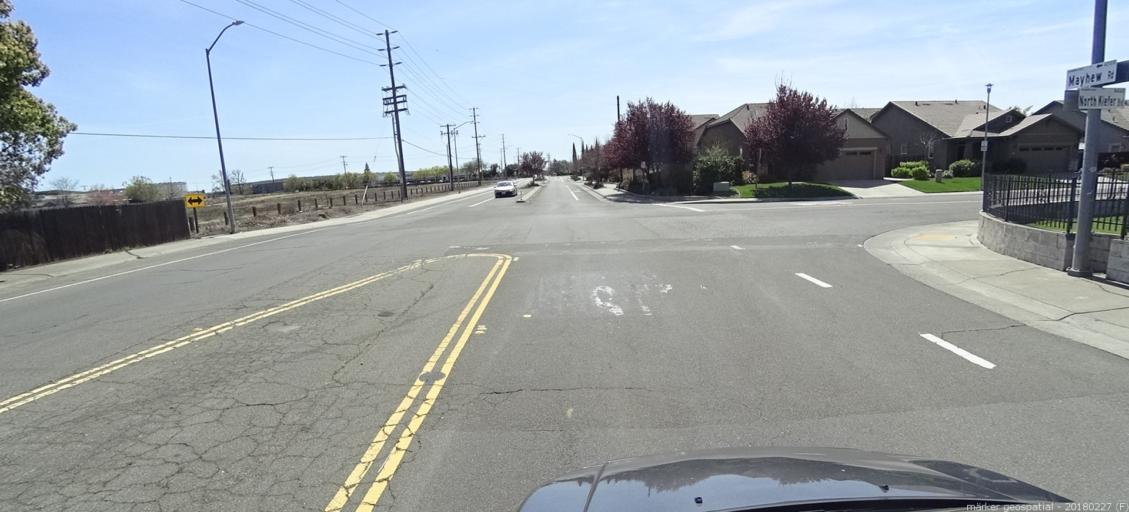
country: US
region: California
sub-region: Sacramento County
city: Rosemont
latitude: 38.5475
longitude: -121.3442
